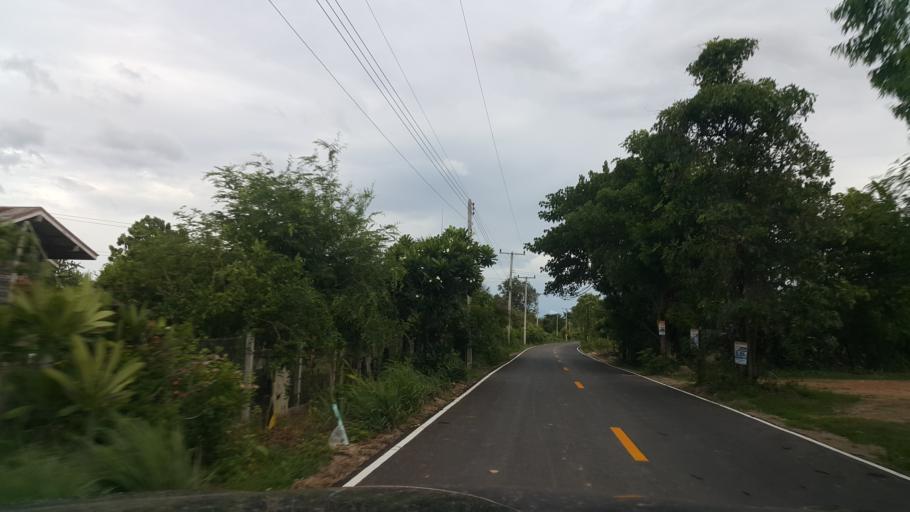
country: TH
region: Sukhothai
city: Thung Saliam
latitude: 17.1684
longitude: 99.4917
